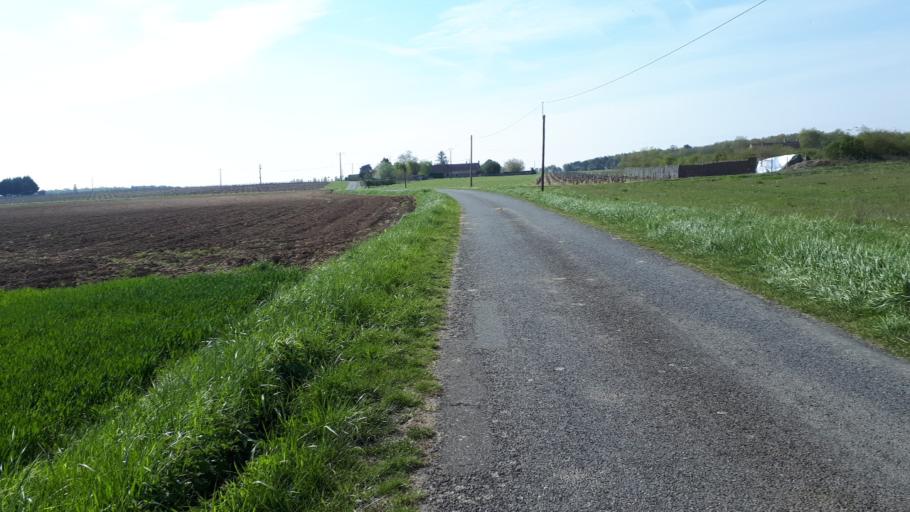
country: FR
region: Centre
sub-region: Departement du Loir-et-Cher
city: Saint-Romain-sur-Cher
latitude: 47.3693
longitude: 1.3895
